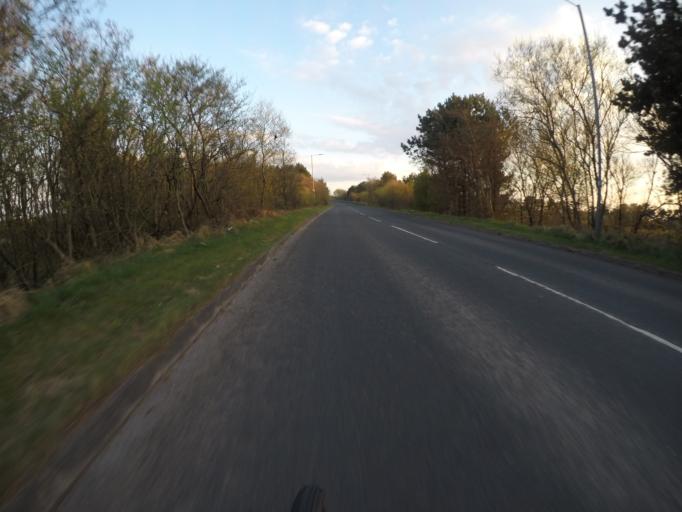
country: GB
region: Scotland
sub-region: North Ayrshire
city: Irvine
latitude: 55.5926
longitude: -4.6678
